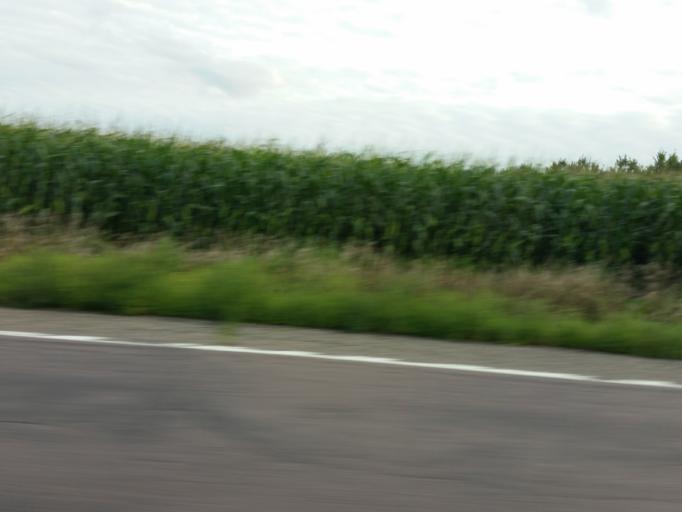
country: US
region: Minnesota
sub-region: Dakota County
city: Farmington
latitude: 44.6305
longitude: -93.0854
